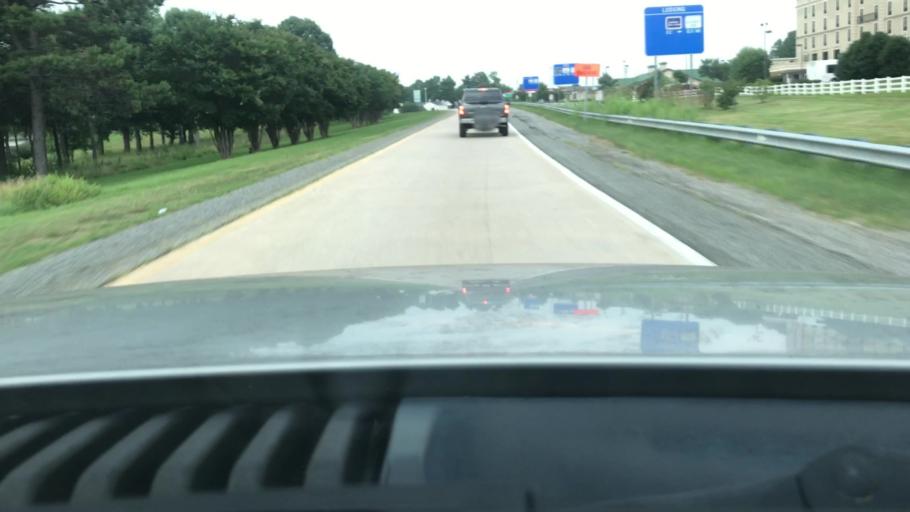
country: US
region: North Carolina
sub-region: Surry County
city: Dobson
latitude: 36.3925
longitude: -80.7872
